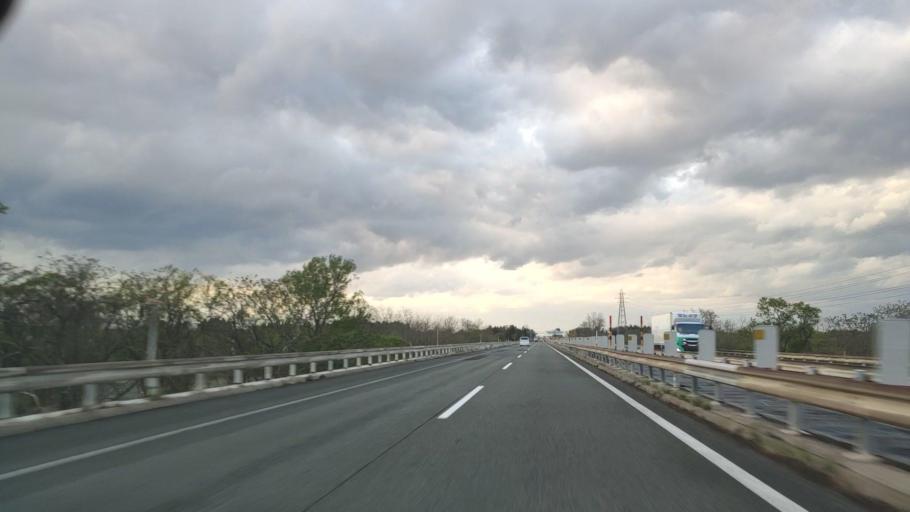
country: JP
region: Iwate
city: Kitakami
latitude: 39.2851
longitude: 141.0817
